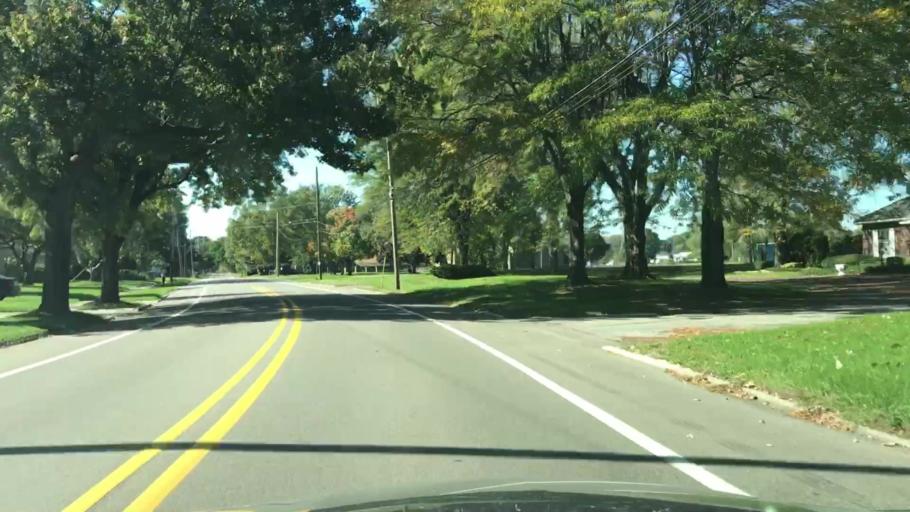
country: US
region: Michigan
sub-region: Macomb County
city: Center Line
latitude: 42.5277
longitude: -83.0544
